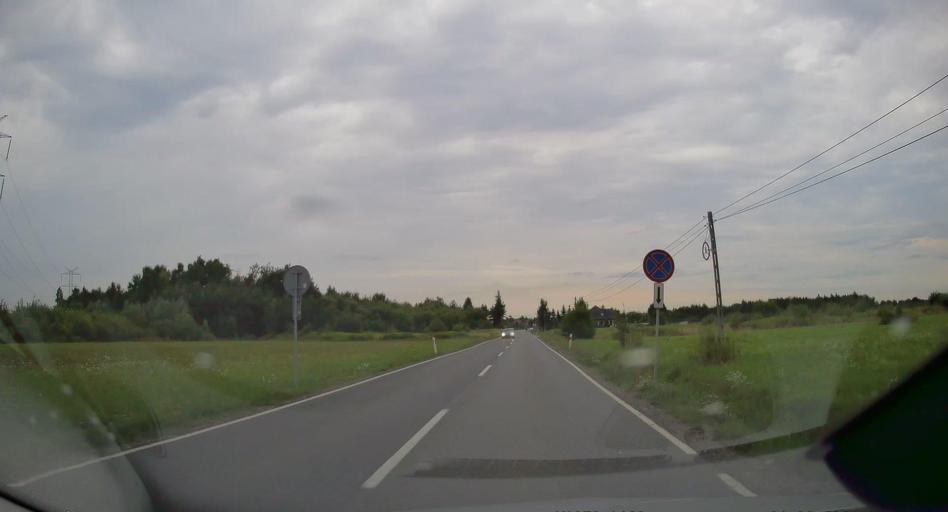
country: PL
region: Lesser Poland Voivodeship
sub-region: Powiat tarnowski
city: Wojnicz
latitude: 49.9853
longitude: 20.8399
